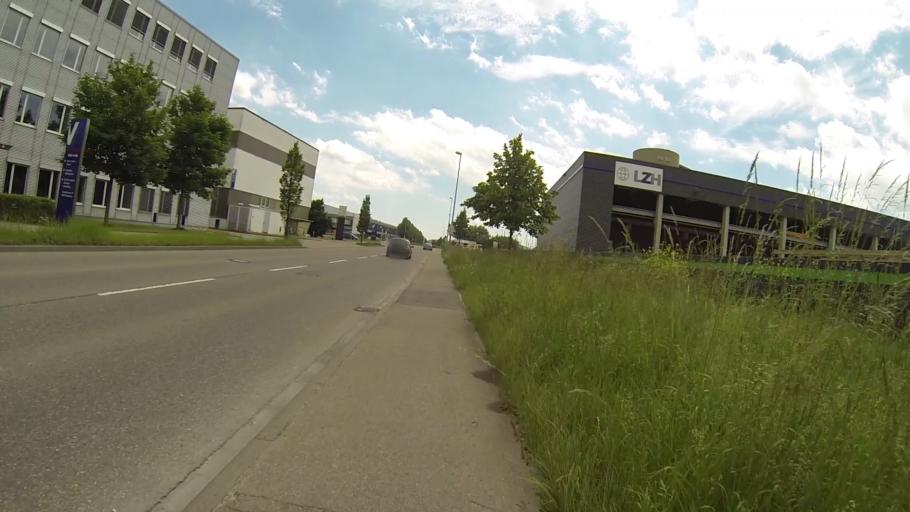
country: DE
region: Baden-Wuerttemberg
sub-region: Regierungsbezirk Stuttgart
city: Bolheim
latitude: 48.6518
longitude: 10.1587
